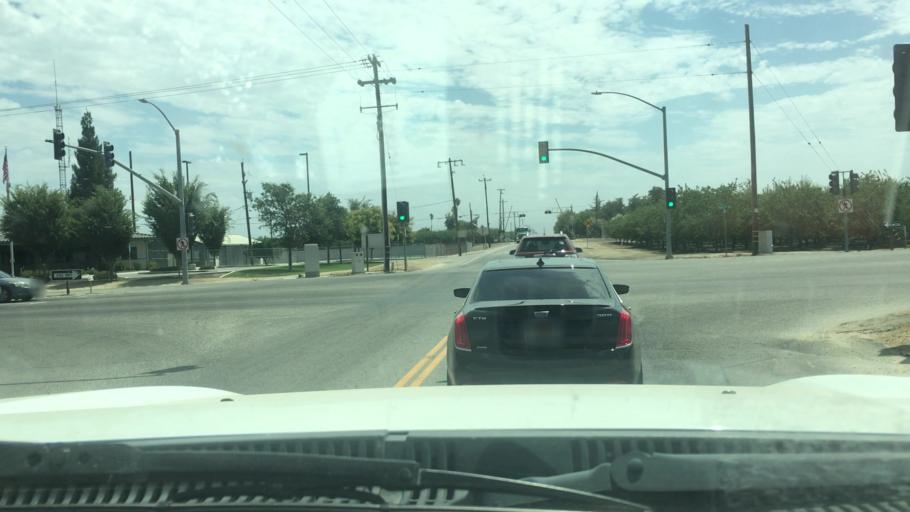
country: US
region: California
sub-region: Kern County
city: Wasco
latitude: 35.5580
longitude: -119.3326
